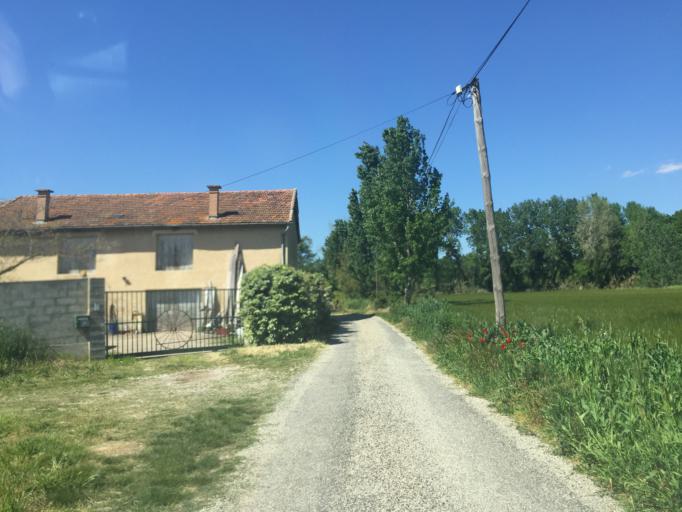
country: FR
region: Provence-Alpes-Cote d'Azur
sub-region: Departement du Vaucluse
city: Orange
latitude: 44.1469
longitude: 4.7790
